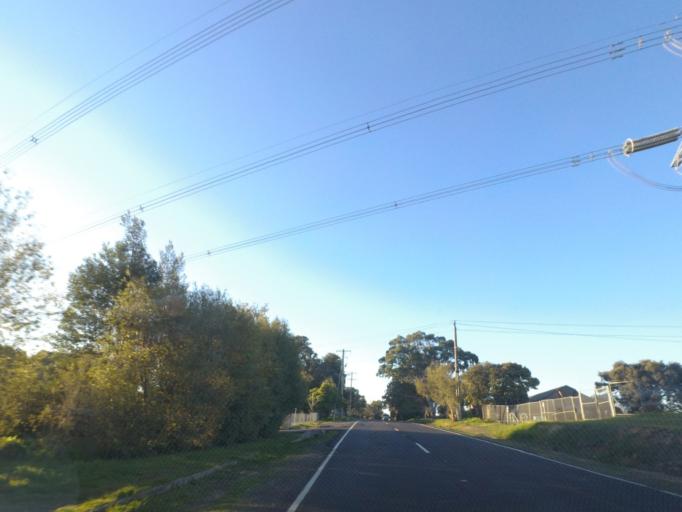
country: AU
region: Victoria
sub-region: Manningham
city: Park Orchards
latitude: -37.7601
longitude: 145.1963
